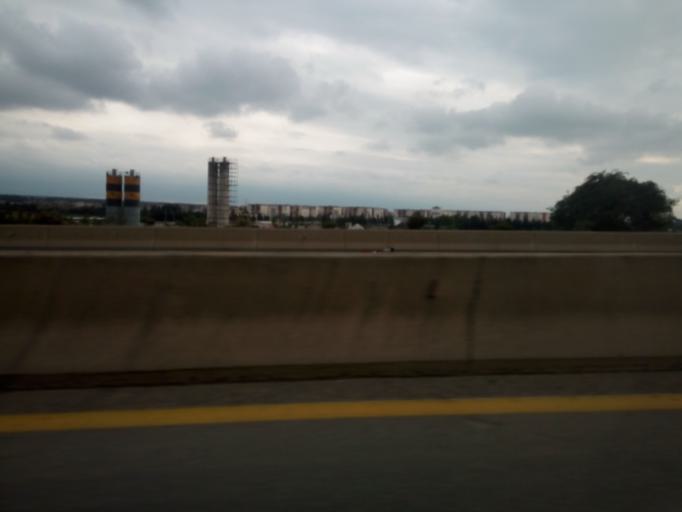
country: DZ
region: Tipaza
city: Saoula
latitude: 36.6500
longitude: 3.0157
